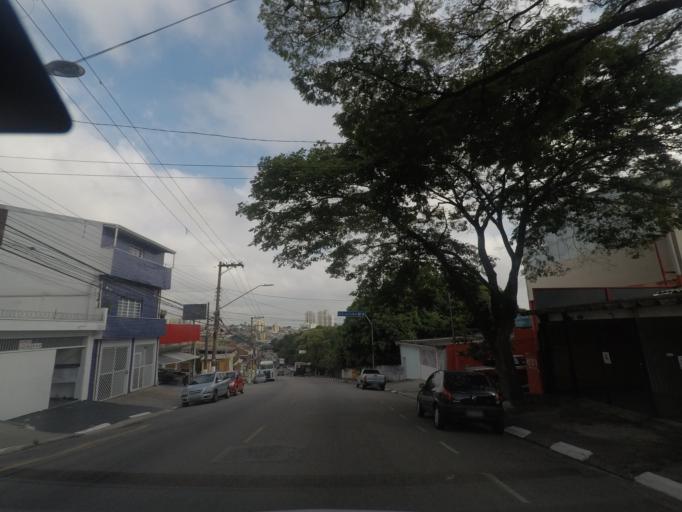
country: BR
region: Sao Paulo
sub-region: Osasco
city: Osasco
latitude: -23.5687
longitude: -46.7791
